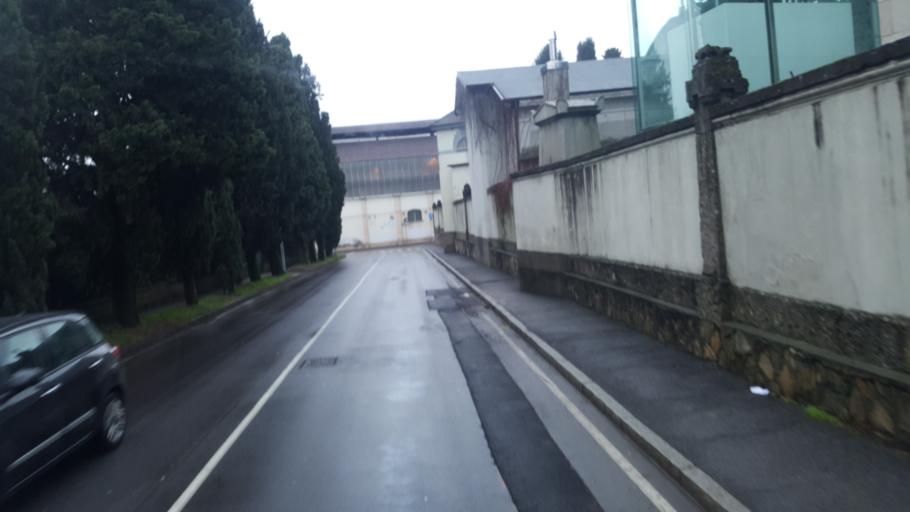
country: IT
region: Lombardy
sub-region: Provincia di Bergamo
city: Bergamo
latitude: 45.6987
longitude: 9.6888
